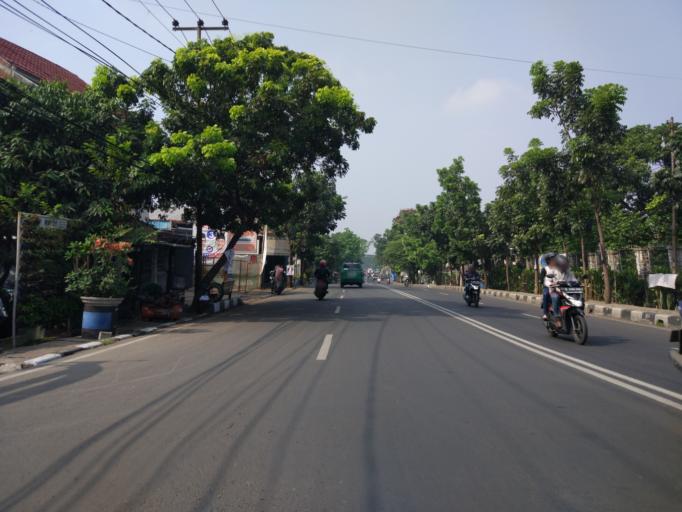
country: ID
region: West Java
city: Cileunyi
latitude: -6.9231
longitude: 107.7101
